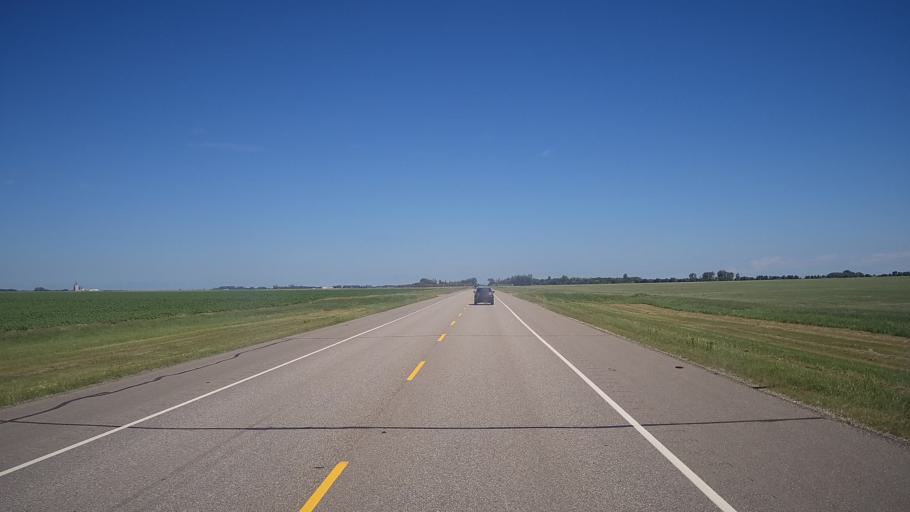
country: CA
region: Manitoba
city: Portage la Prairie
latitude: 50.0397
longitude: -98.4688
